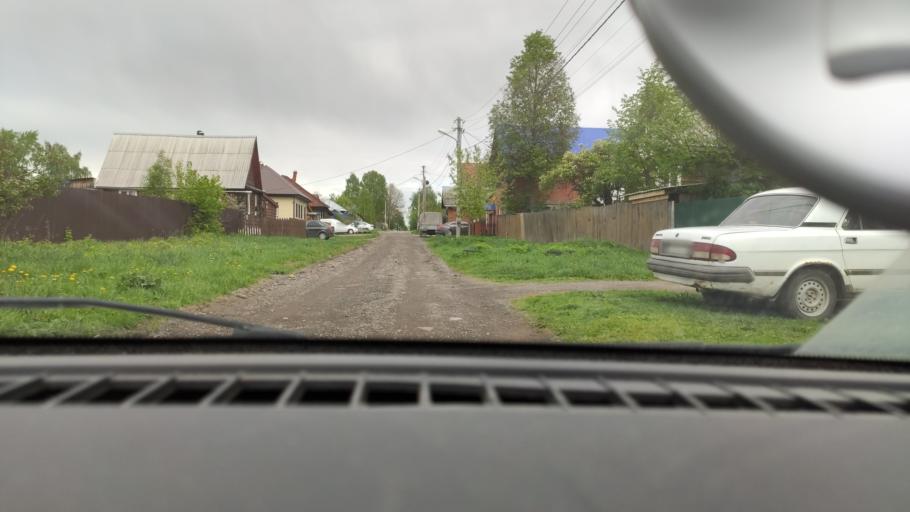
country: RU
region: Perm
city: Perm
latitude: 58.0206
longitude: 56.3270
